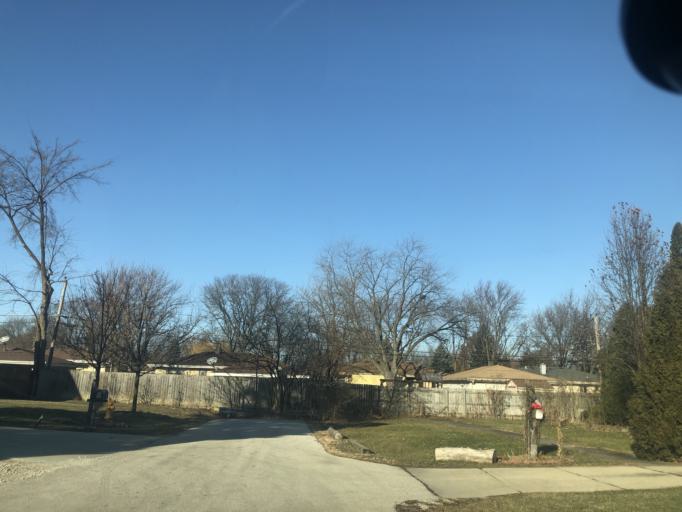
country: US
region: Illinois
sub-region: DuPage County
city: Addison
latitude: 41.9427
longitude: -88.0062
